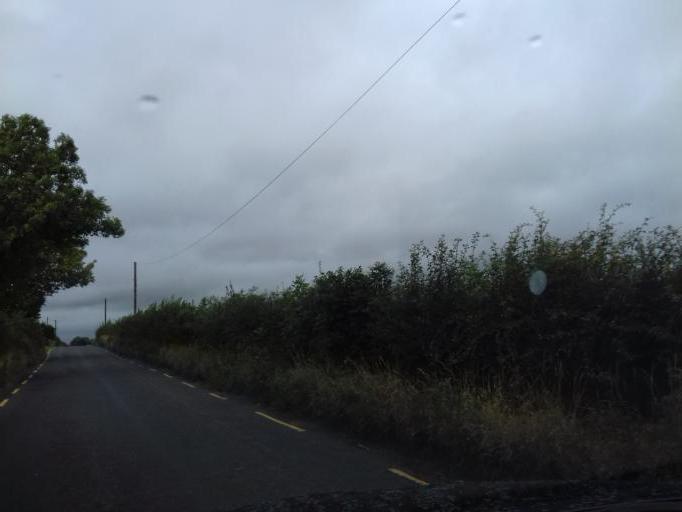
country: IE
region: Leinster
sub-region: Kilkenny
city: Graiguenamanagh
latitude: 52.6124
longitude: -7.0317
